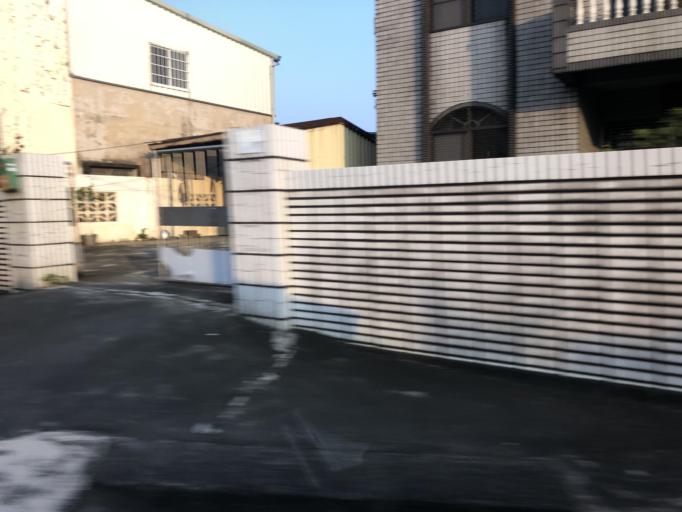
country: TW
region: Taiwan
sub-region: Tainan
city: Tainan
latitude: 23.1452
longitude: 120.2694
